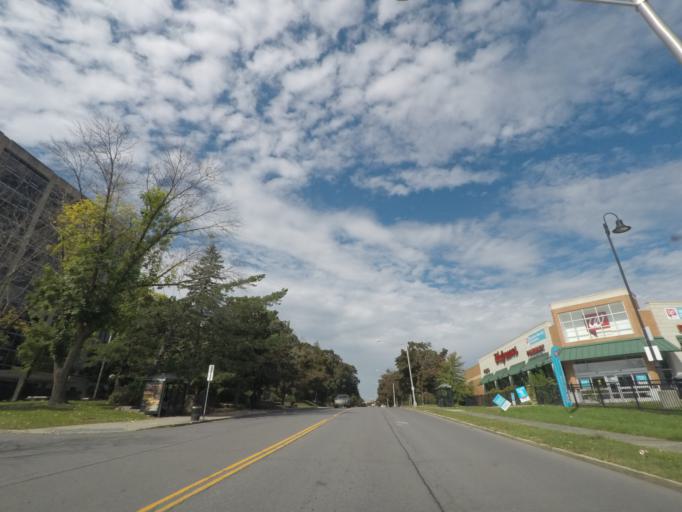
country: US
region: New York
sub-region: Albany County
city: Albany
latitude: 42.6479
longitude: -73.7731
